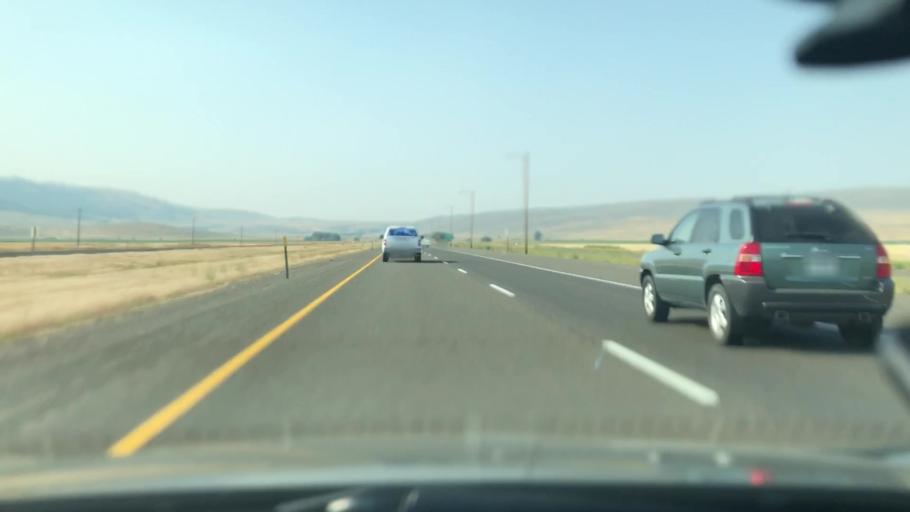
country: US
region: Oregon
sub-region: Union County
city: Union
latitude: 45.1048
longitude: -117.9556
